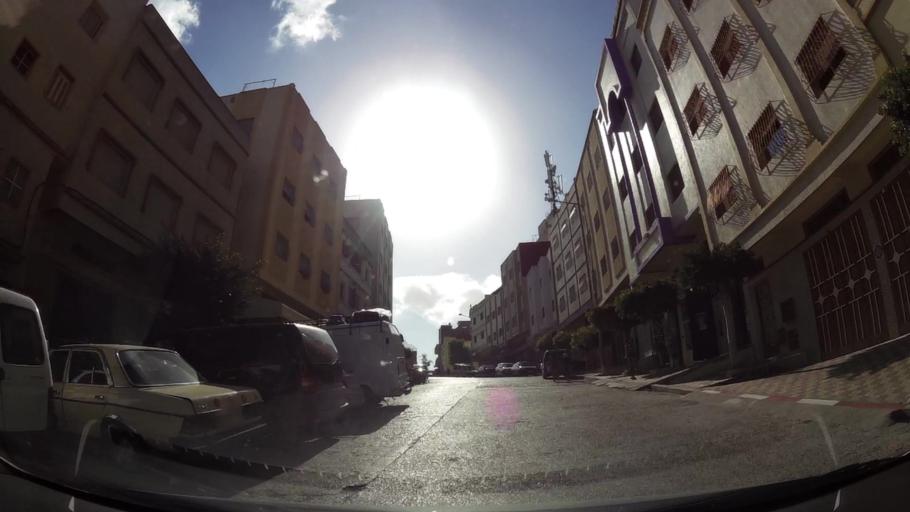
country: MA
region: Tanger-Tetouan
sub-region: Tanger-Assilah
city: Tangier
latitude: 35.7472
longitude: -5.8046
